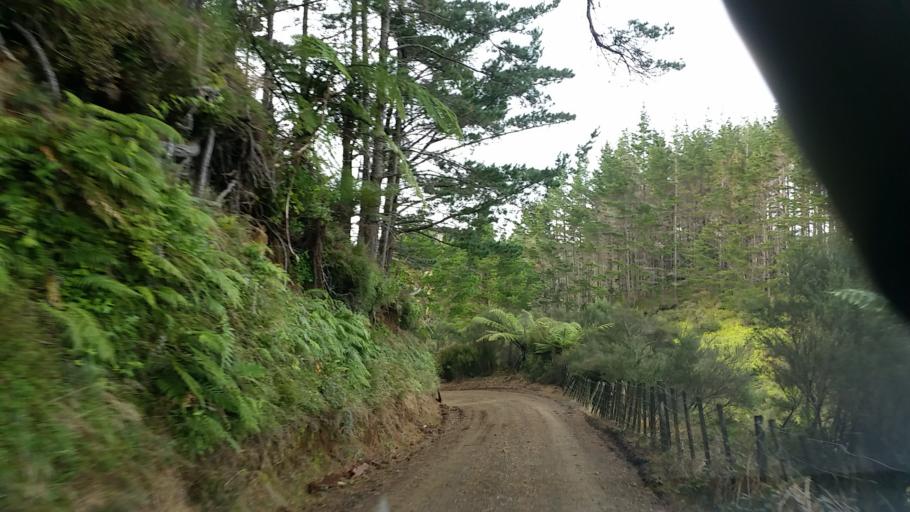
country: NZ
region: Taranaki
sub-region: New Plymouth District
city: Waitara
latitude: -39.0437
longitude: 174.4224
